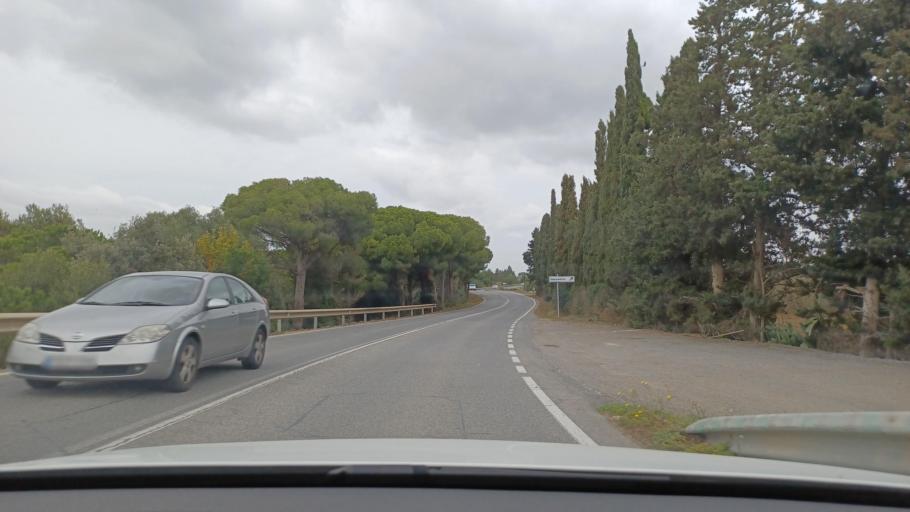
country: ES
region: Catalonia
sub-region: Provincia de Tarragona
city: Cambrils
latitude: 41.0887
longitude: 1.0801
